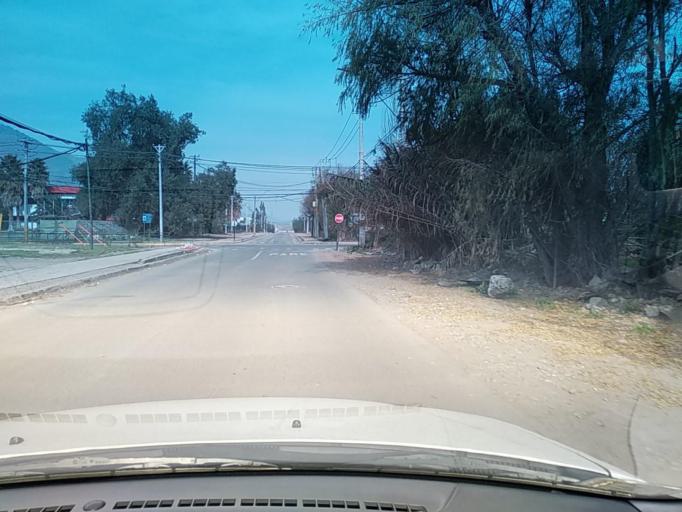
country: CL
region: Santiago Metropolitan
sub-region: Provincia de Chacabuco
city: Chicureo Abajo
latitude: -33.3097
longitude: -70.7154
